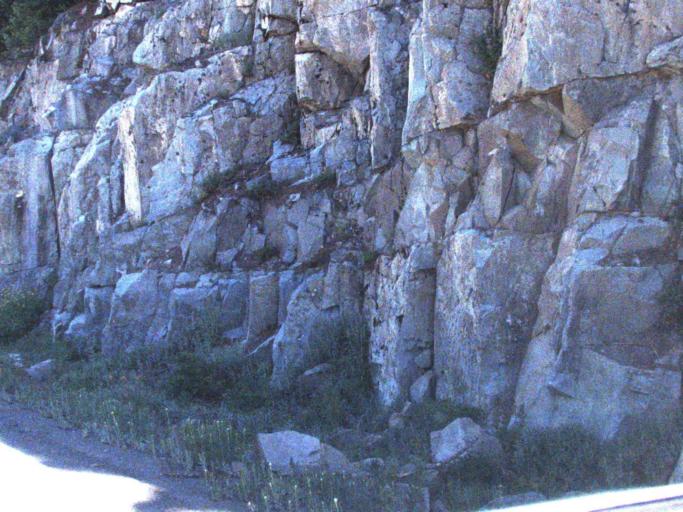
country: US
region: Washington
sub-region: King County
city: Enumclaw
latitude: 46.8703
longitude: -121.5268
